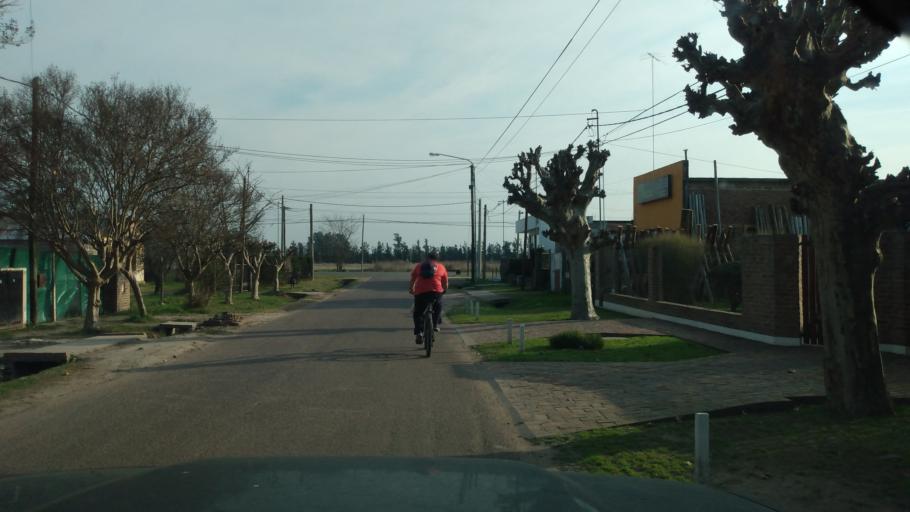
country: AR
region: Buenos Aires
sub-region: Partido de Lujan
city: Lujan
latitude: -34.5808
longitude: -59.1783
